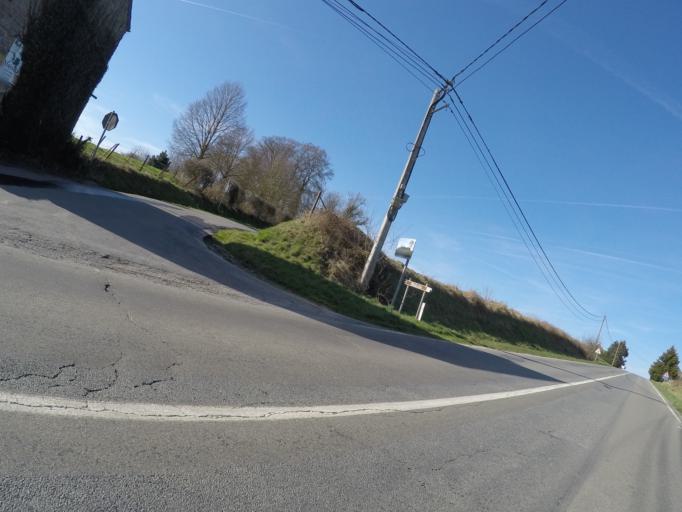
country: BE
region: Wallonia
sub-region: Province de Namur
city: Hamois
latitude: 50.3530
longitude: 5.1065
